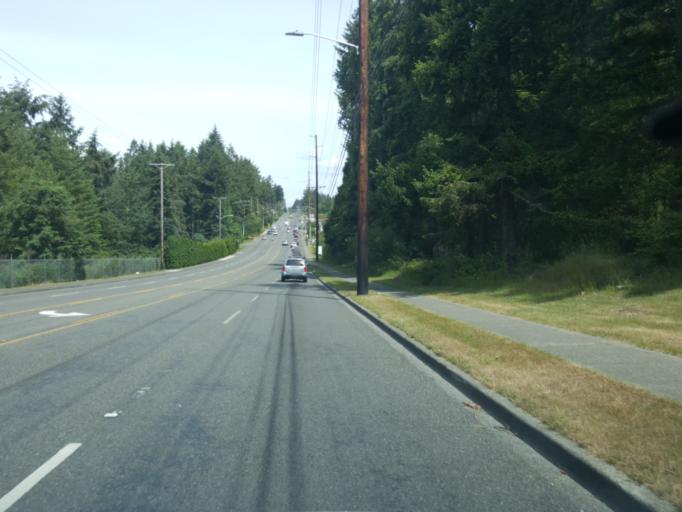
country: US
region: Washington
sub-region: Pierce County
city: Fircrest
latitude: 47.2295
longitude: -122.5051
